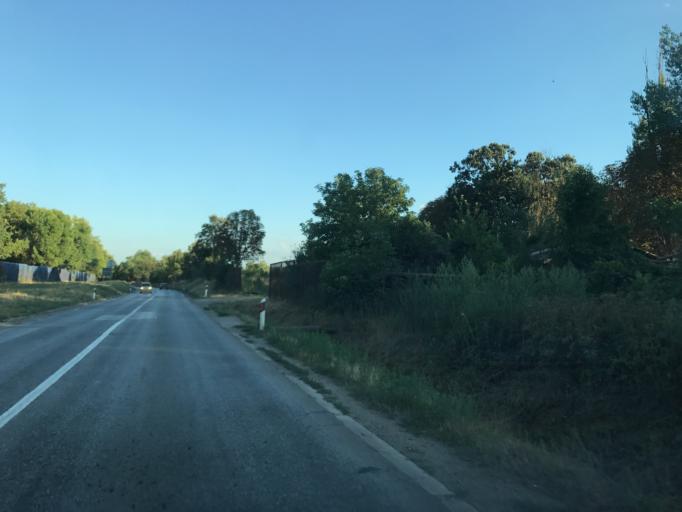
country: RS
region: Central Serbia
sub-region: Podunavski Okrug
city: Smederevo
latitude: 44.6002
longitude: 20.9639
